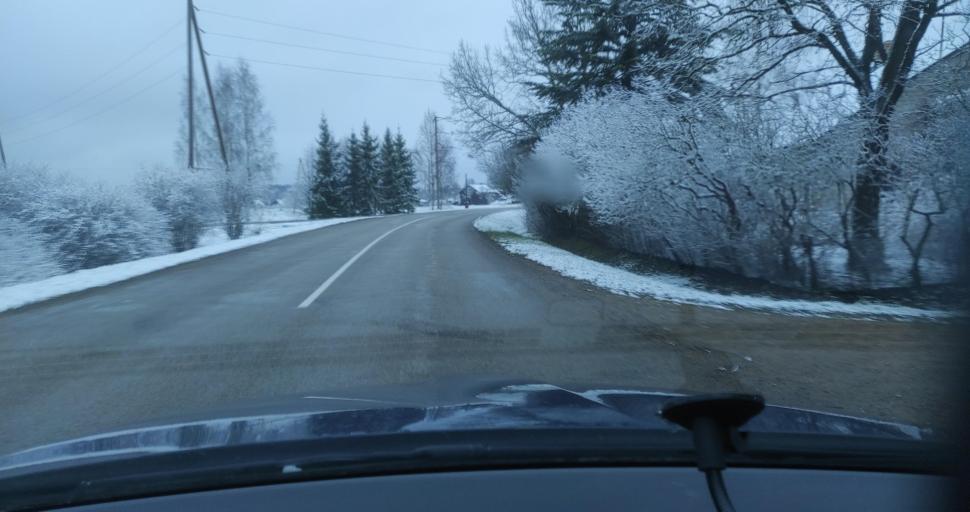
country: LV
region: Skrunda
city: Skrunda
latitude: 56.8663
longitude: 22.2320
